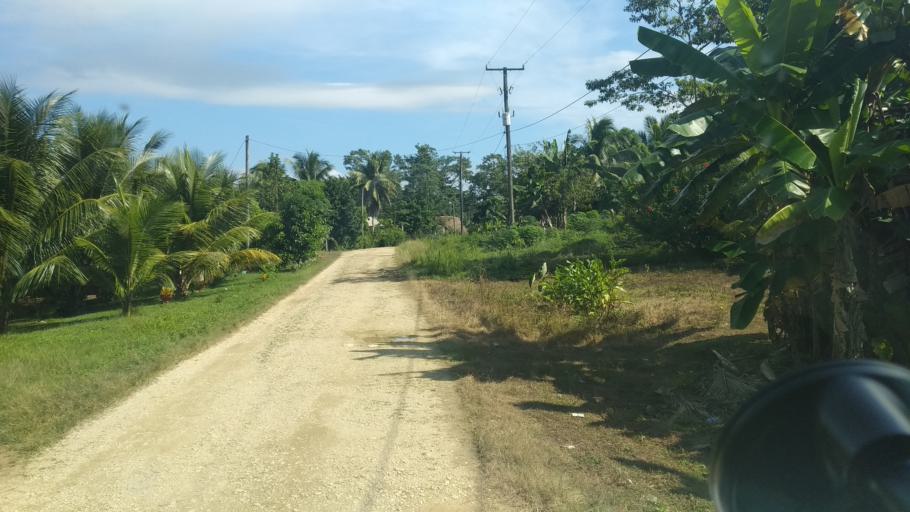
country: BZ
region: Toledo
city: Punta Gorda
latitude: 16.2182
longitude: -88.9019
